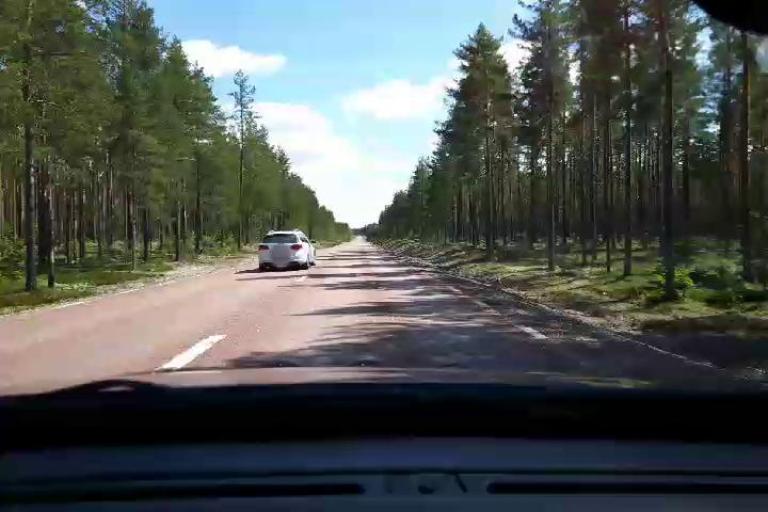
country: SE
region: Gaevleborg
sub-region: Ljusdals Kommun
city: Farila
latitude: 61.8147
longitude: 15.7643
